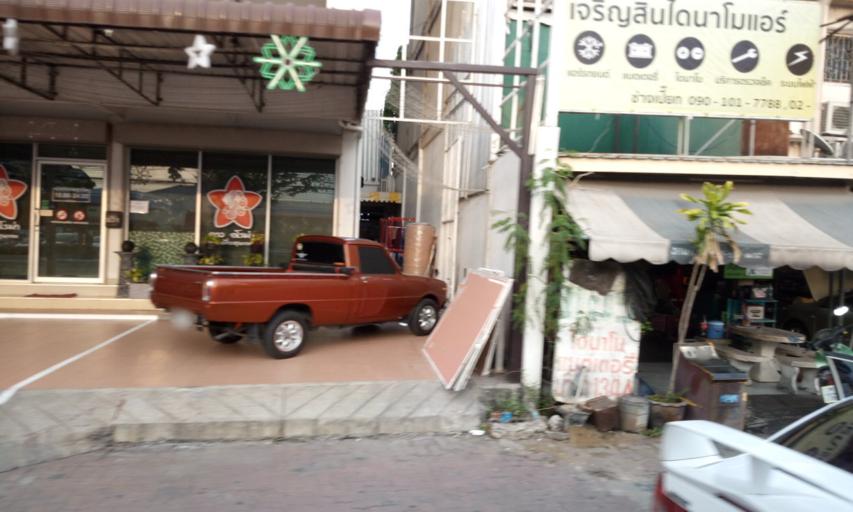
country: TH
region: Bangkok
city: Lat Phrao
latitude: 13.8150
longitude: 100.6107
